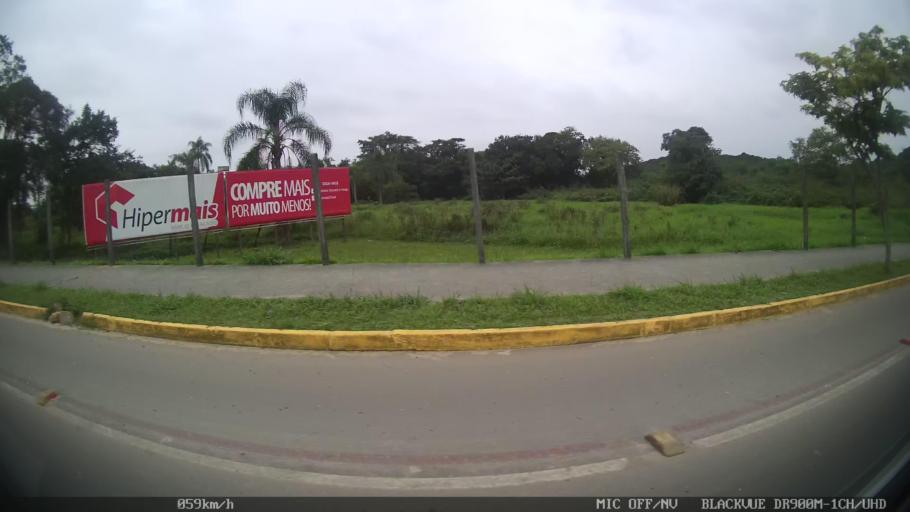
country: BR
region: Santa Catarina
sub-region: Joinville
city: Joinville
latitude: -26.3512
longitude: -48.8391
